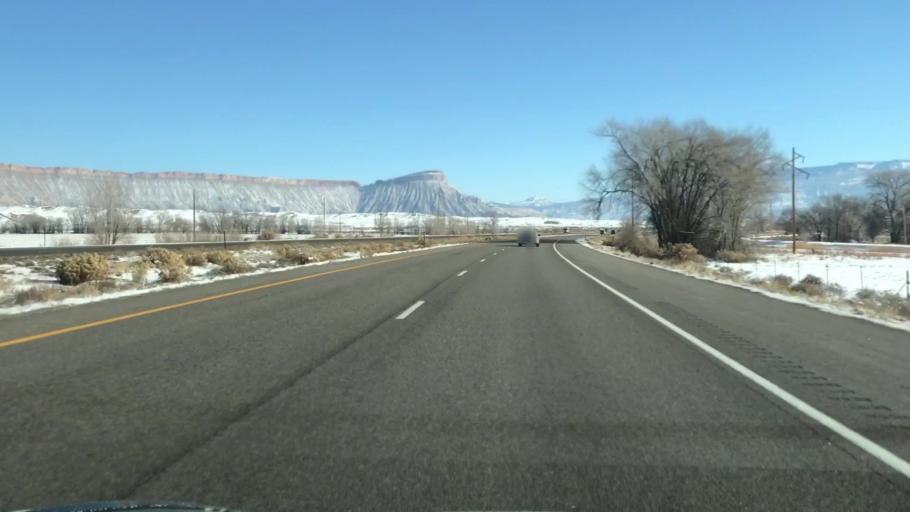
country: US
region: Colorado
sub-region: Mesa County
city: Fruitvale
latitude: 39.1085
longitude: -108.5082
